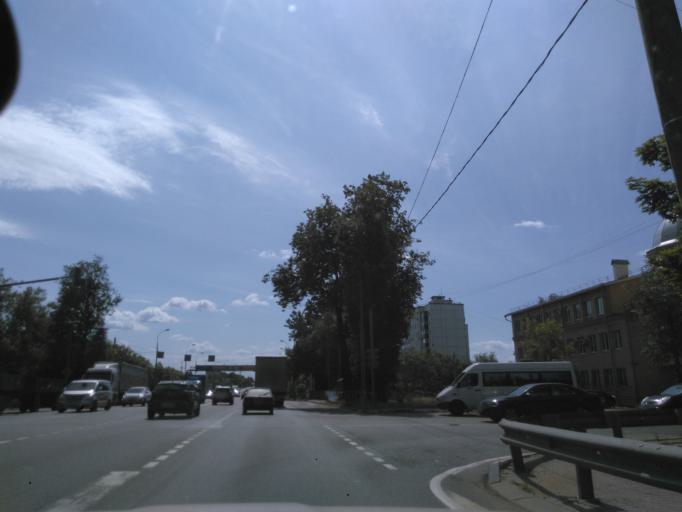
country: RU
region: Moskovskaya
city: Solnechnogorsk
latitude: 56.1844
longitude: 36.9825
